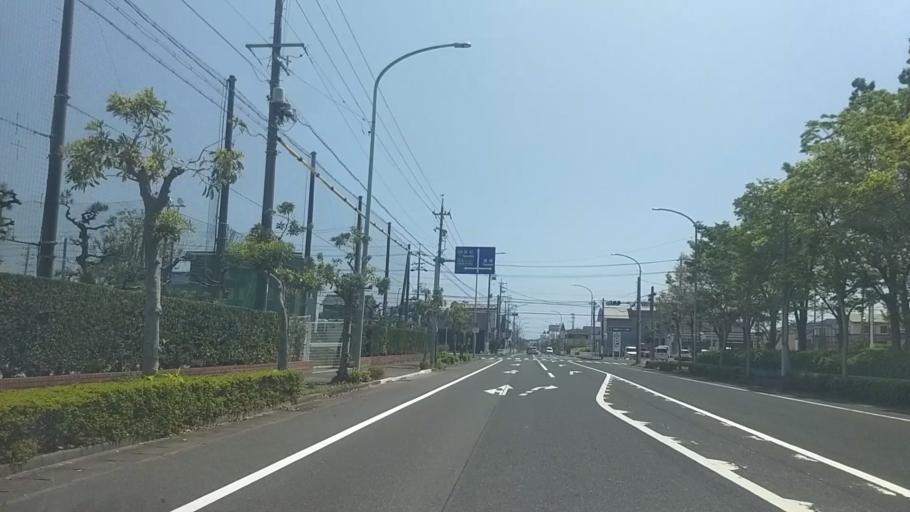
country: JP
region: Shizuoka
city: Kosai-shi
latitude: 34.6902
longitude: 137.5696
